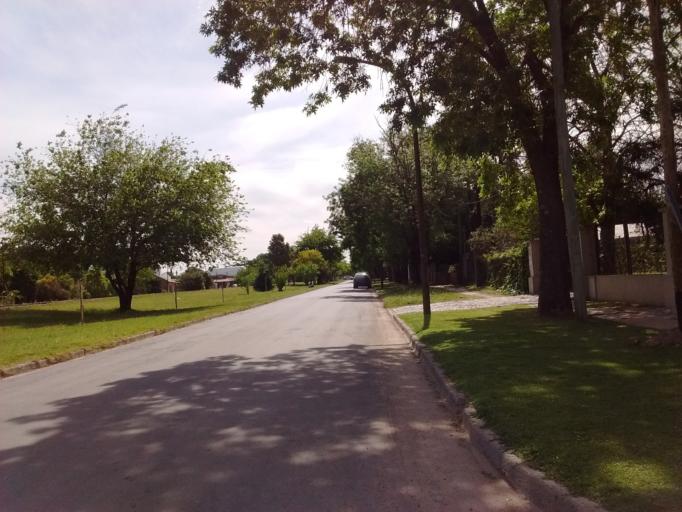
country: AR
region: Santa Fe
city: Funes
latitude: -32.9178
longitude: -60.8049
